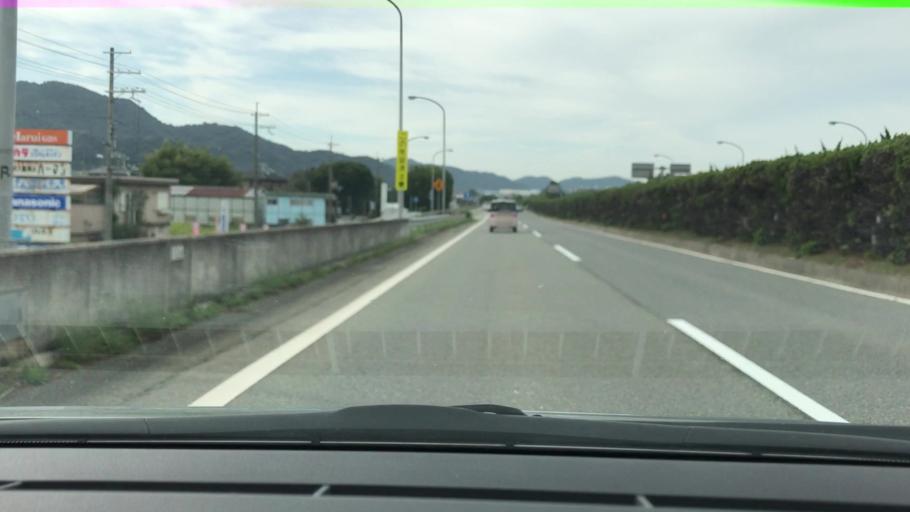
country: JP
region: Hyogo
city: Himeji
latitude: 34.9112
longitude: 134.7545
